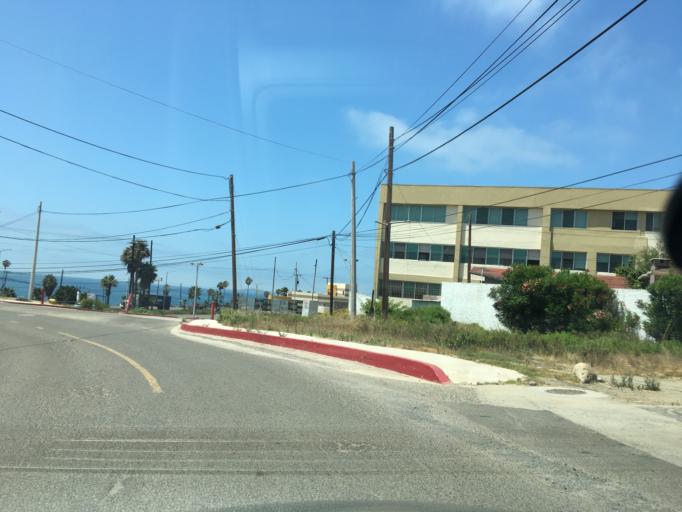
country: MX
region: Baja California
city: El Sauzal
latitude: 31.8675
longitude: -116.6676
